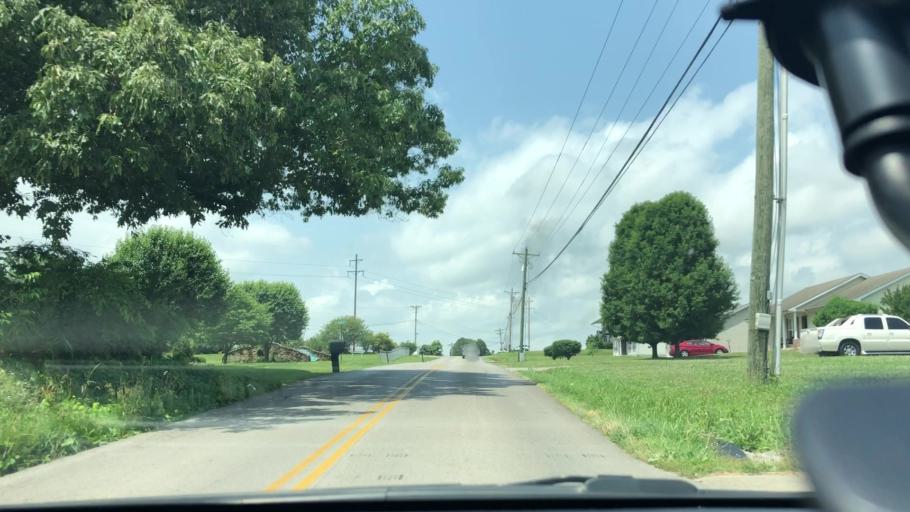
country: US
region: Kentucky
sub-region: Pulaski County
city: Somerset
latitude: 37.0595
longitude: -84.6683
